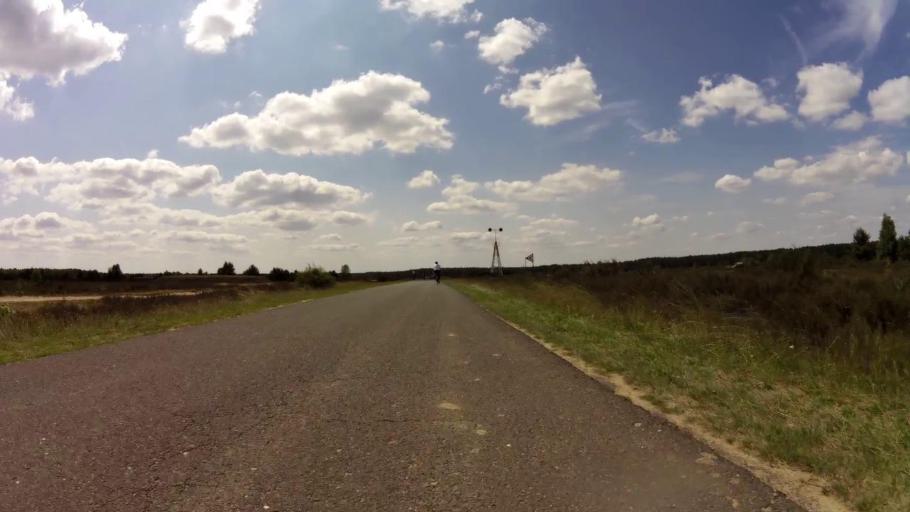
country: PL
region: West Pomeranian Voivodeship
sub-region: Powiat drawski
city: Drawsko Pomorskie
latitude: 53.4194
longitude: 15.7421
